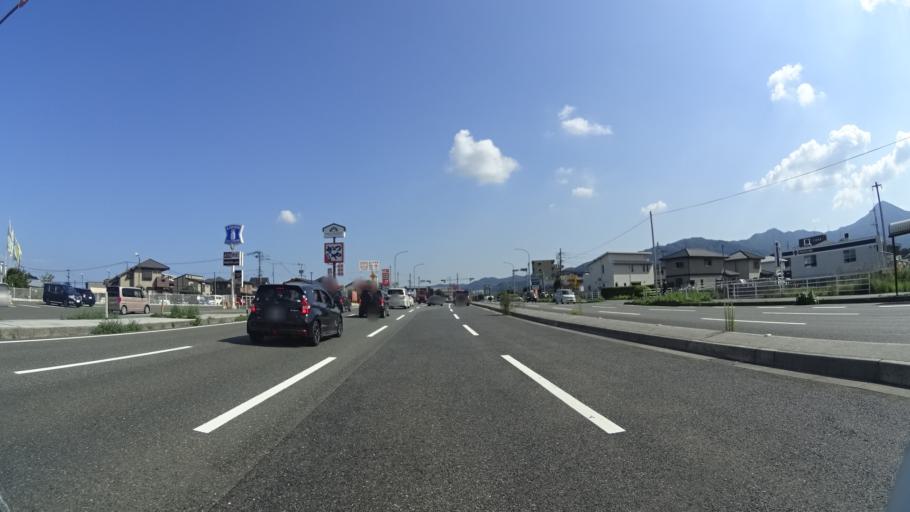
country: JP
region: Fukuoka
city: Kanda
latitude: 33.8246
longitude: 130.9320
